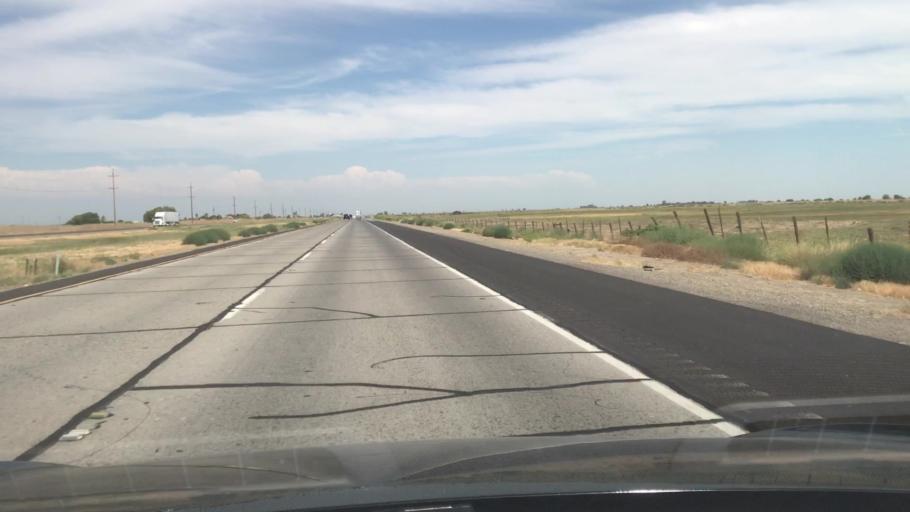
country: US
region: California
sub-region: Merced County
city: Los Banos
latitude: 37.0554
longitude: -120.7752
